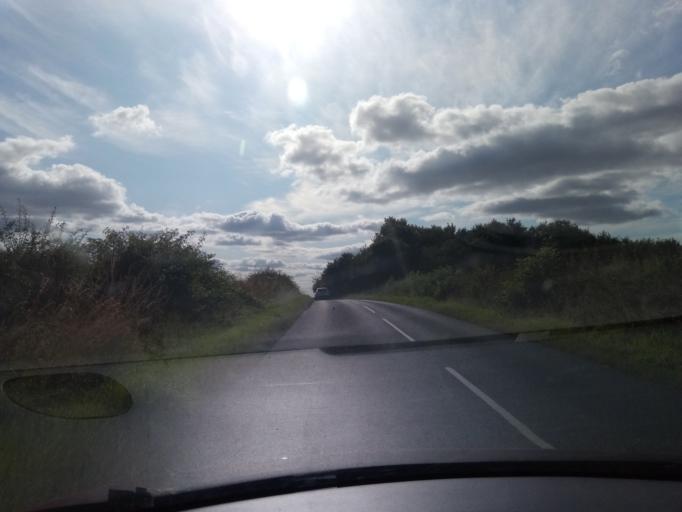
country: GB
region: Scotland
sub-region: The Scottish Borders
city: Allanton
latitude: 55.7370
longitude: -2.2037
